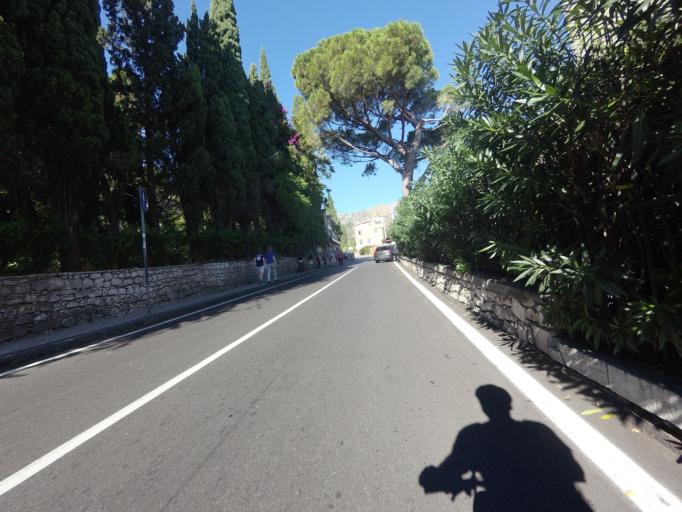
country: IT
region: Sicily
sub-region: Messina
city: Taormina
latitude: 37.8532
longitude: 15.2938
